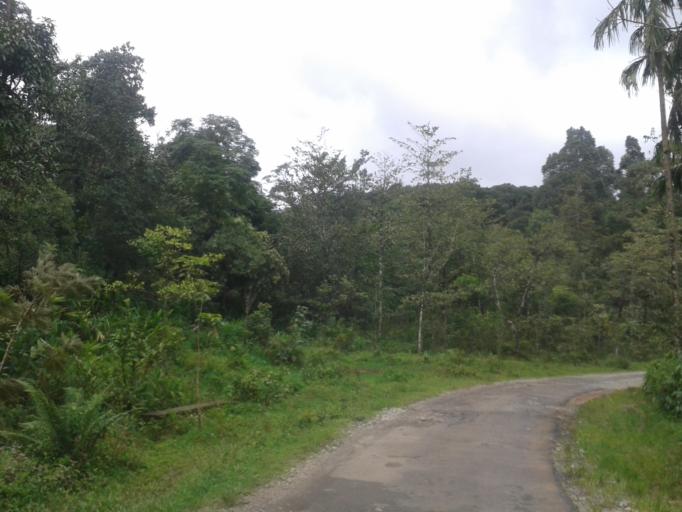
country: IN
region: Karnataka
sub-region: Chikmagalur
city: Mudigere
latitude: 12.9853
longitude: 75.6176
